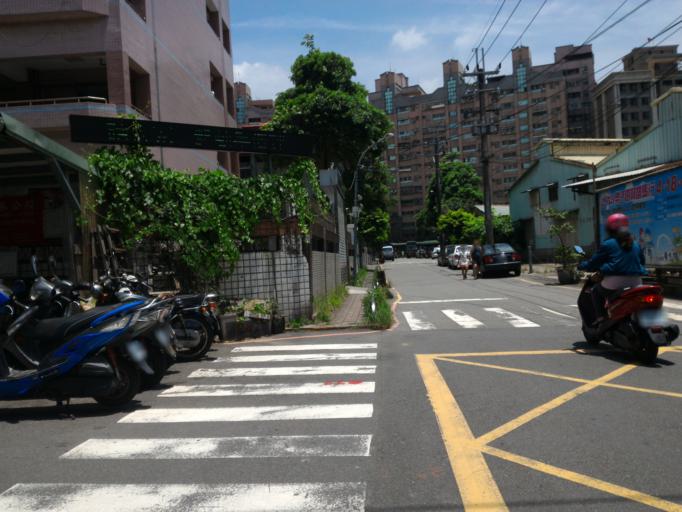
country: TW
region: Taipei
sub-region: Taipei
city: Banqiao
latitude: 24.9821
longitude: 121.4163
